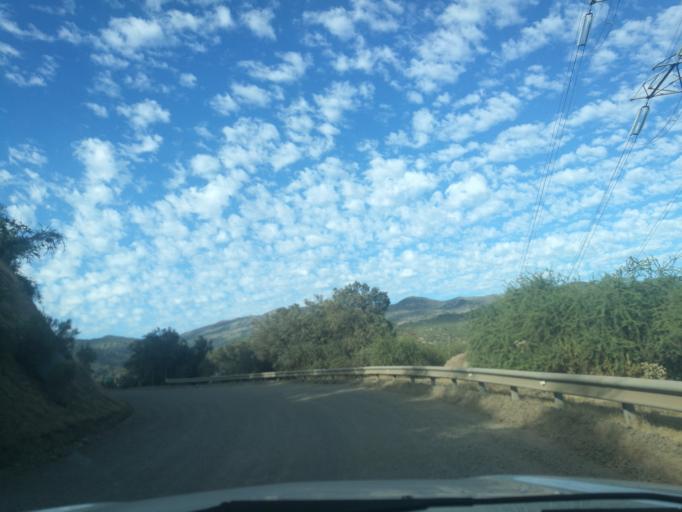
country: CL
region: O'Higgins
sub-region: Provincia de Cachapoal
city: Machali
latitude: -34.2556
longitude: -70.4630
